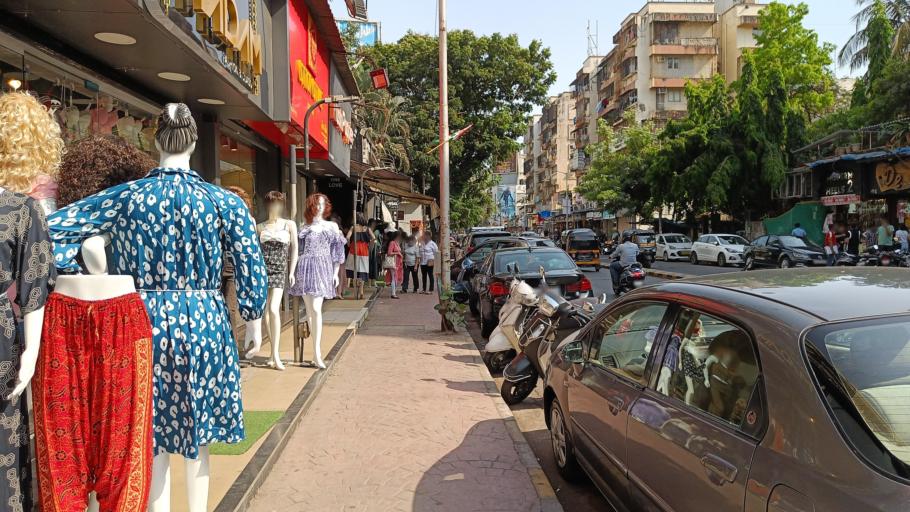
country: IN
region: Maharashtra
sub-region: Mumbai Suburban
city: Powai
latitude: 19.1426
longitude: 72.8248
